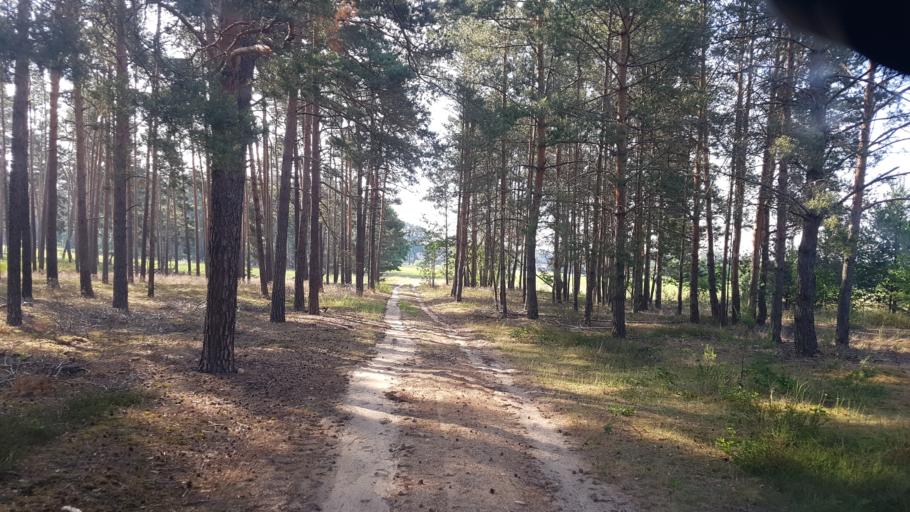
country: DE
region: Brandenburg
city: Finsterwalde
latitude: 51.6146
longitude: 13.6394
